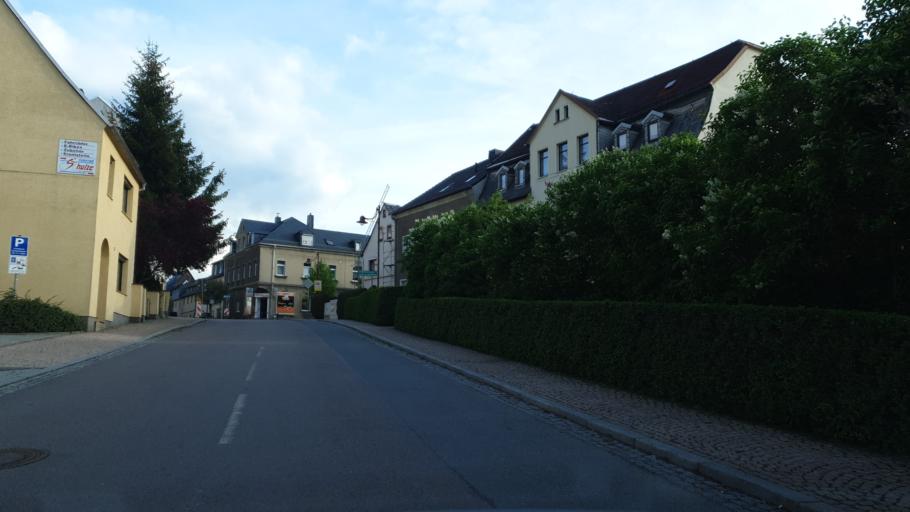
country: DE
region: Saxony
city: Lichtenstein
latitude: 50.7541
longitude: 12.6329
